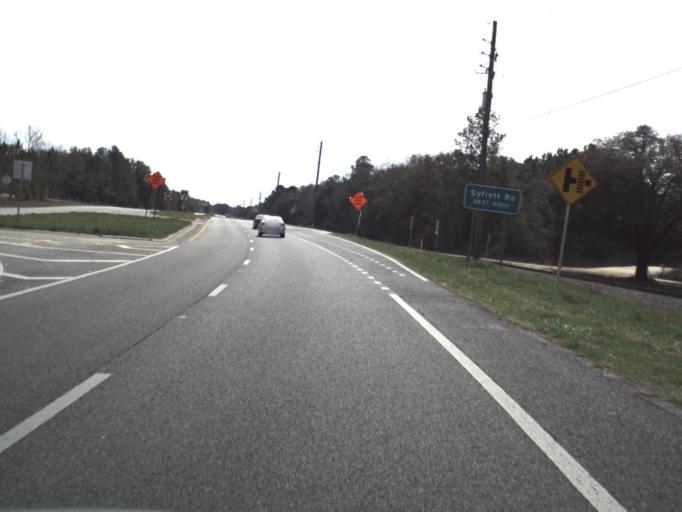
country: US
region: Florida
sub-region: Washington County
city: Chipley
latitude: 30.7201
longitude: -85.3901
